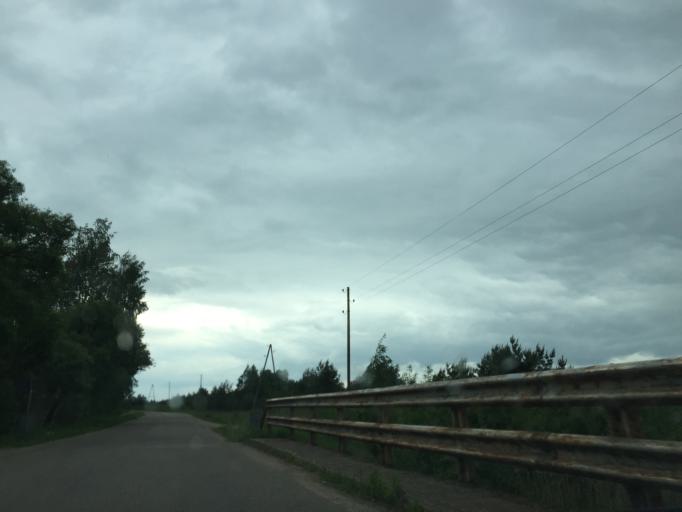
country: LV
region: Aglona
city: Aglona
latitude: 56.0583
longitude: 26.8048
